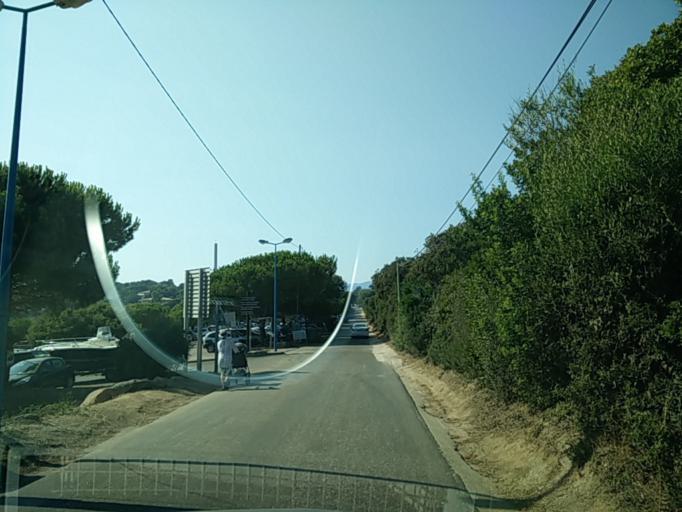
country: FR
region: Corsica
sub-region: Departement de la Corse-du-Sud
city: Pietrosella
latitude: 41.8429
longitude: 8.7672
